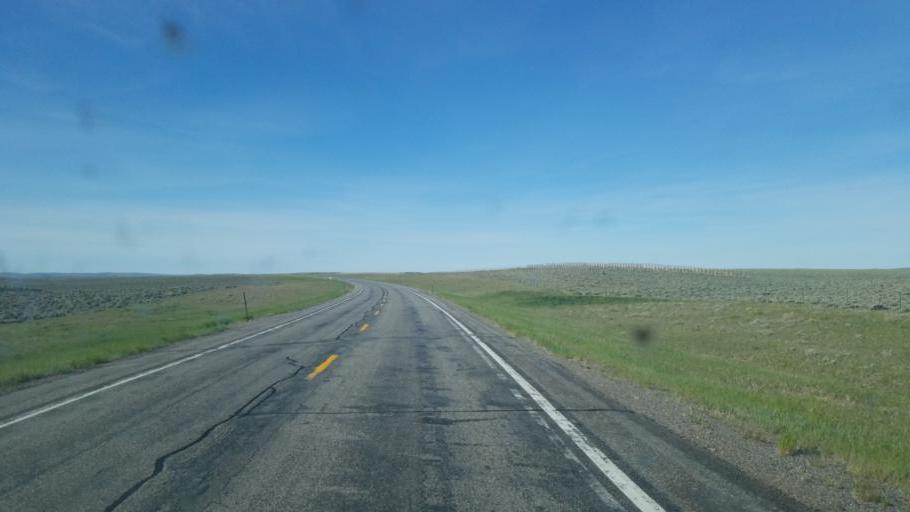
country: US
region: Wyoming
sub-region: Fremont County
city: Riverton
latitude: 42.6482
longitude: -108.1927
